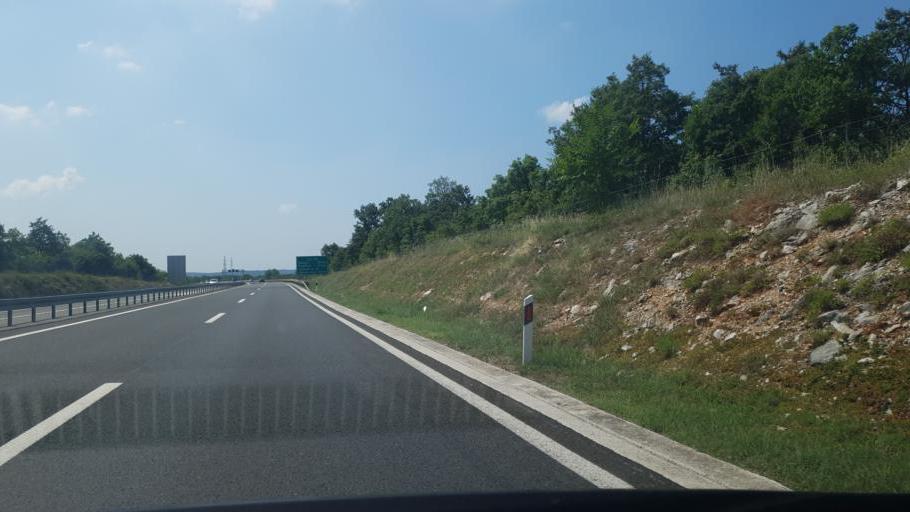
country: HR
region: Istarska
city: Vodnjan
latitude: 45.1048
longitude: 13.8177
